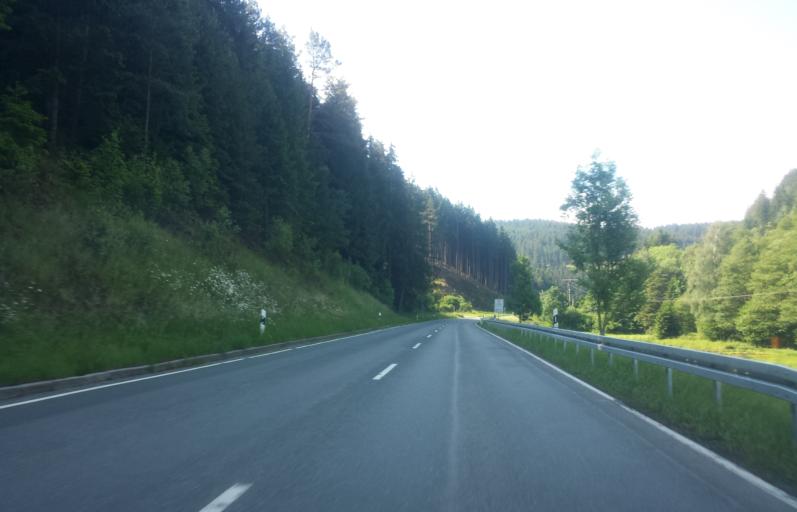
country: DE
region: Bavaria
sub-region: Upper Franconia
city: Ludwigsstadt
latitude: 50.4767
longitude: 11.3947
